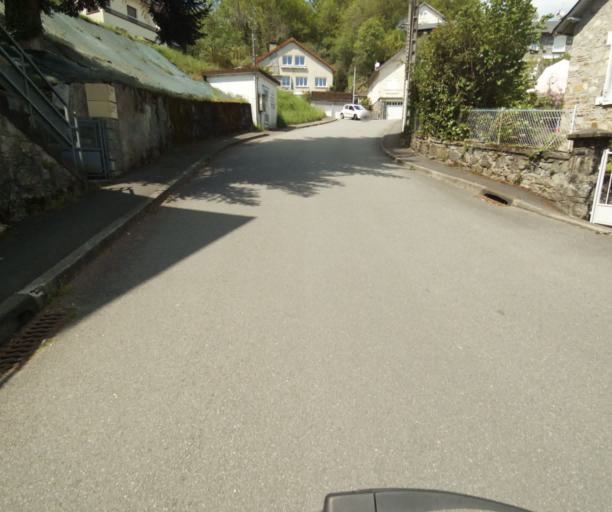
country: FR
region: Limousin
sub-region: Departement de la Correze
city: Tulle
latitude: 45.2701
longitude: 1.7650
